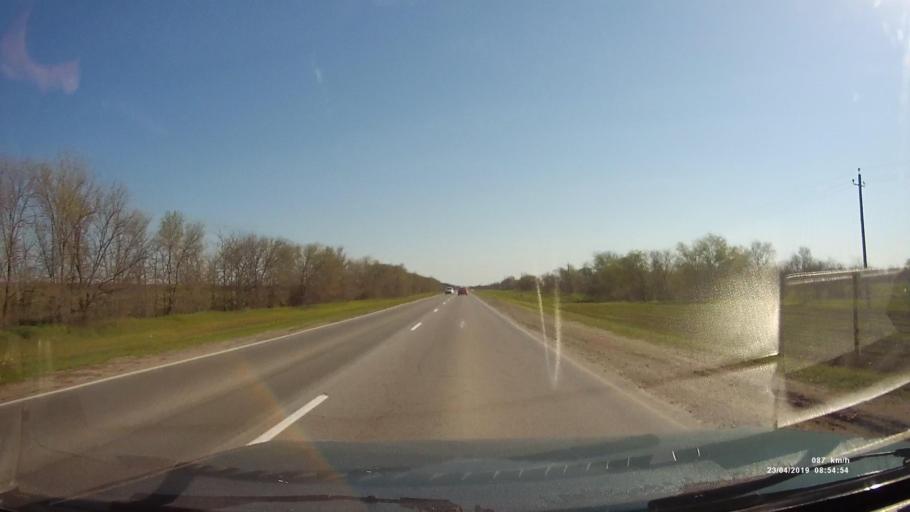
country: RU
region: Rostov
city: Sal'sk
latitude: 46.4803
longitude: 41.4808
